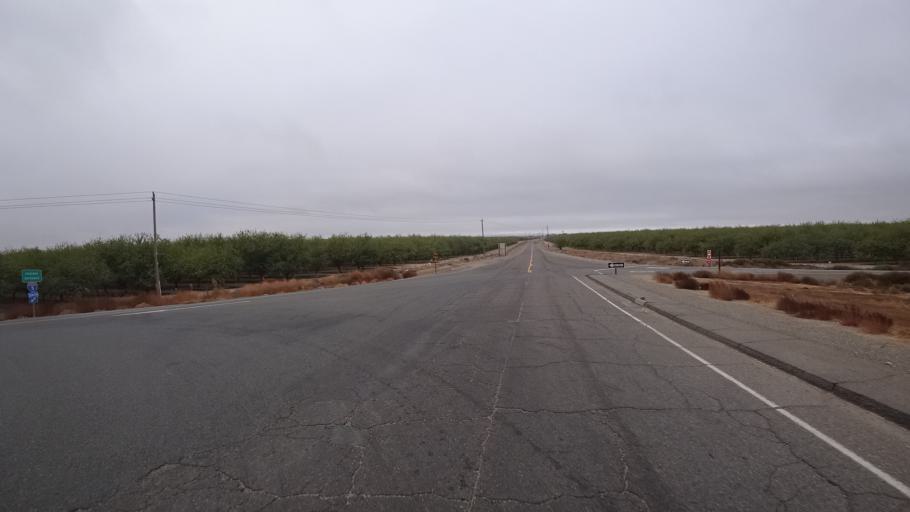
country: US
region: California
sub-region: Yolo County
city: Dunnigan
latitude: 38.9256
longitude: -122.0019
